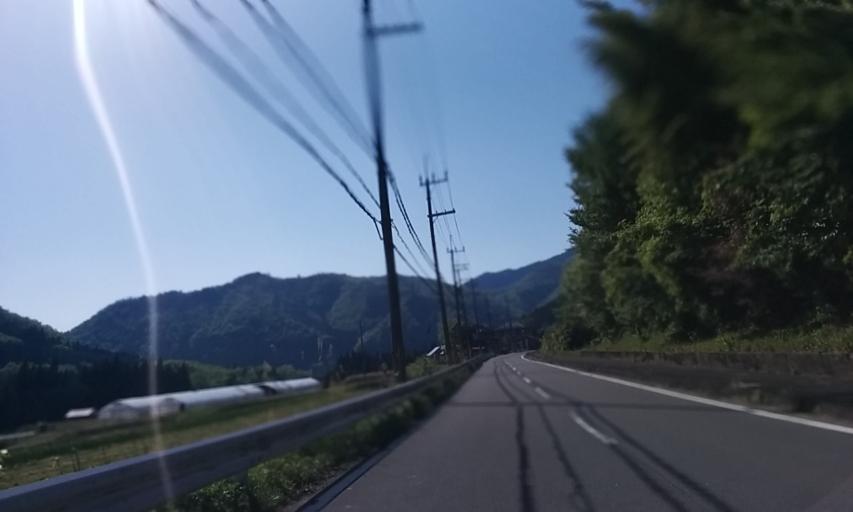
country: JP
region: Kyoto
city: Ayabe
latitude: 35.2619
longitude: 135.4434
